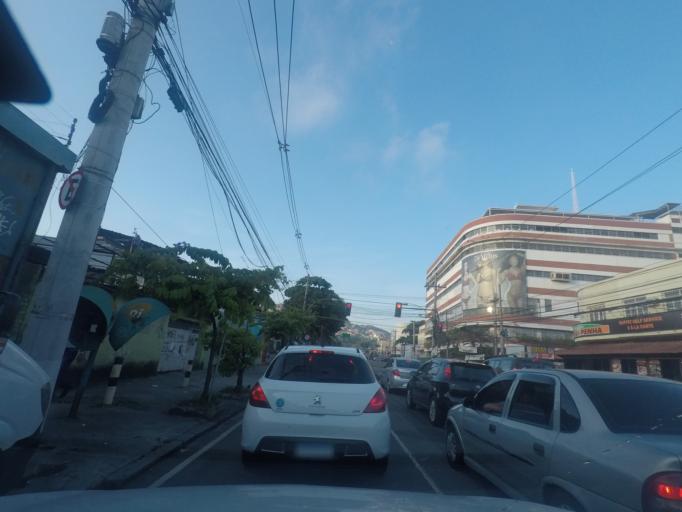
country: BR
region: Rio de Janeiro
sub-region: Duque De Caxias
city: Duque de Caxias
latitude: -22.8341
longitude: -43.2812
